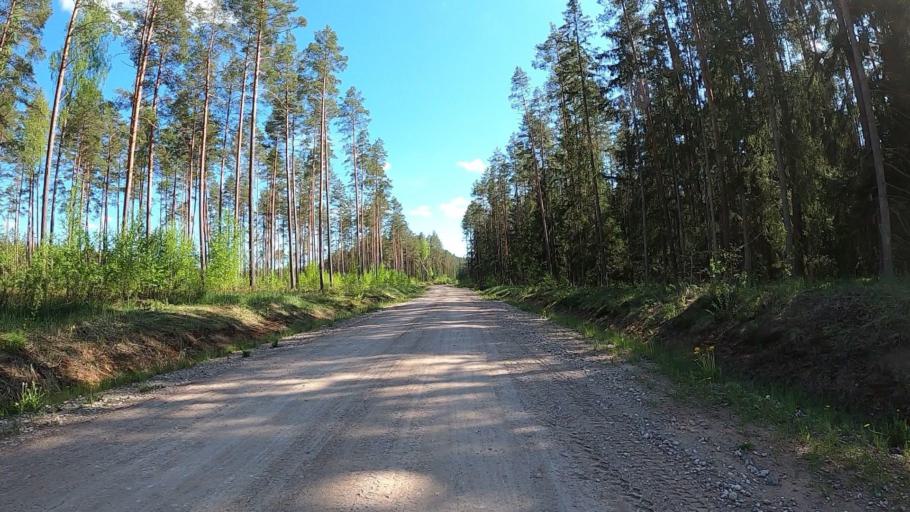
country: LV
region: Baldone
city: Baldone
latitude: 56.7752
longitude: 24.3745
